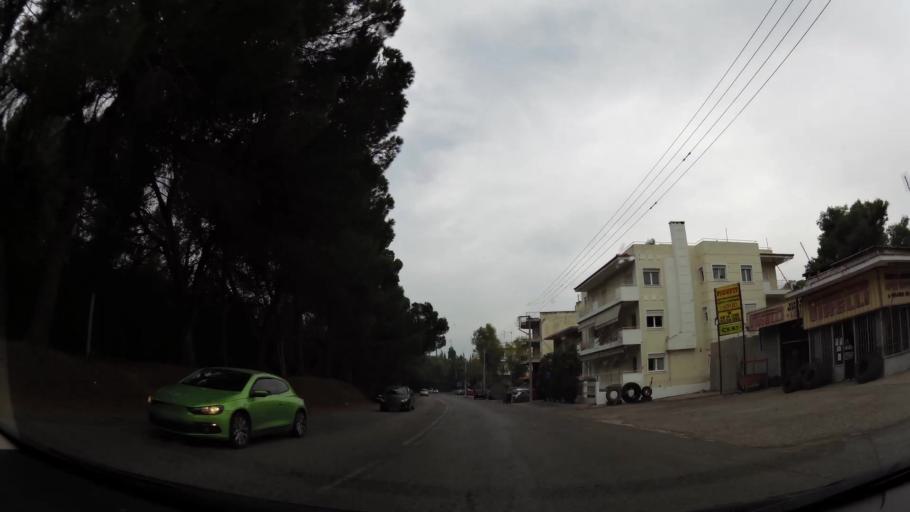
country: GR
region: Attica
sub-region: Nomarchia Athinas
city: Chaidari
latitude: 38.0099
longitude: 23.6475
